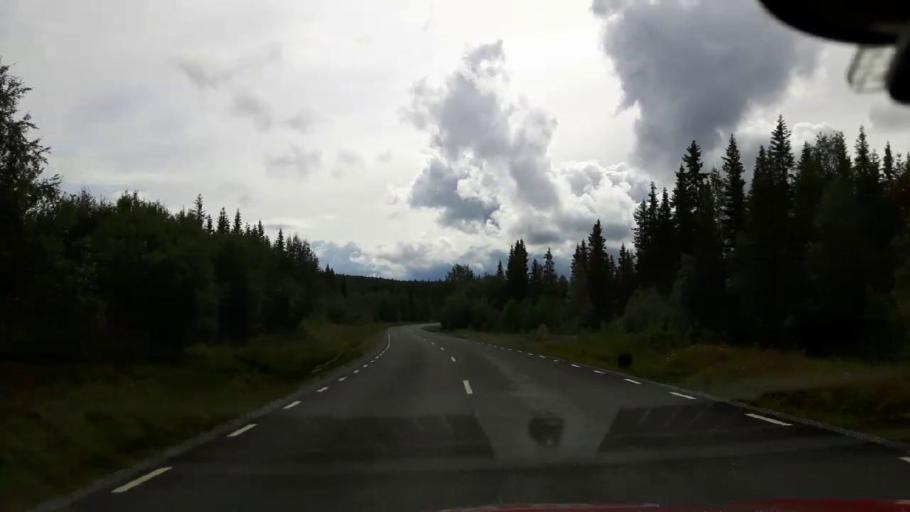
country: NO
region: Nord-Trondelag
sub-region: Lierne
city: Sandvika
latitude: 64.6191
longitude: 14.1222
